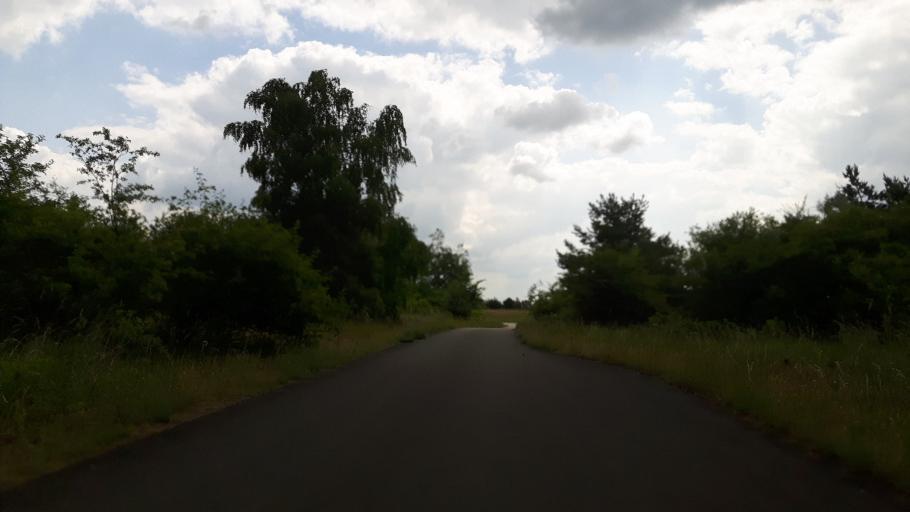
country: DE
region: Saxony-Anhalt
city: Pouch
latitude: 51.5952
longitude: 12.4126
